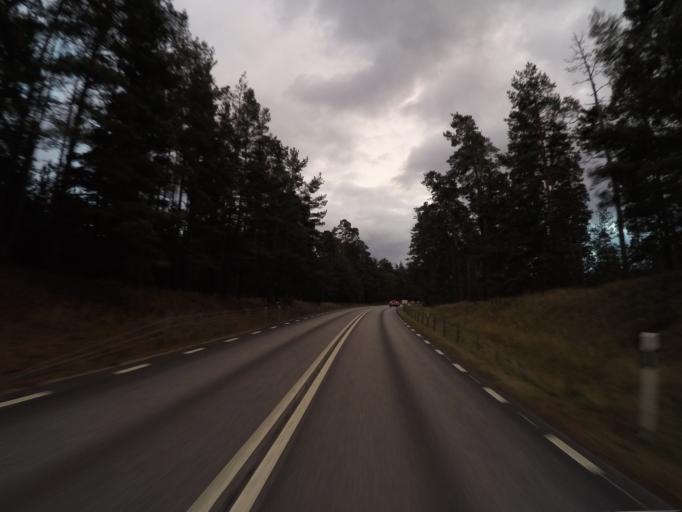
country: SE
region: Skane
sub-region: Kristianstads Kommun
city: Degeberga
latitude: 55.8752
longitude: 14.0888
